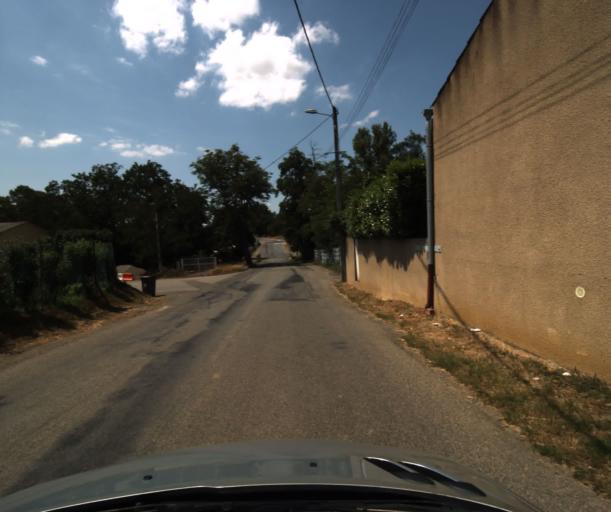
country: FR
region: Midi-Pyrenees
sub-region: Departement de la Haute-Garonne
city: Saint-Lys
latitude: 43.5123
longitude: 1.1734
